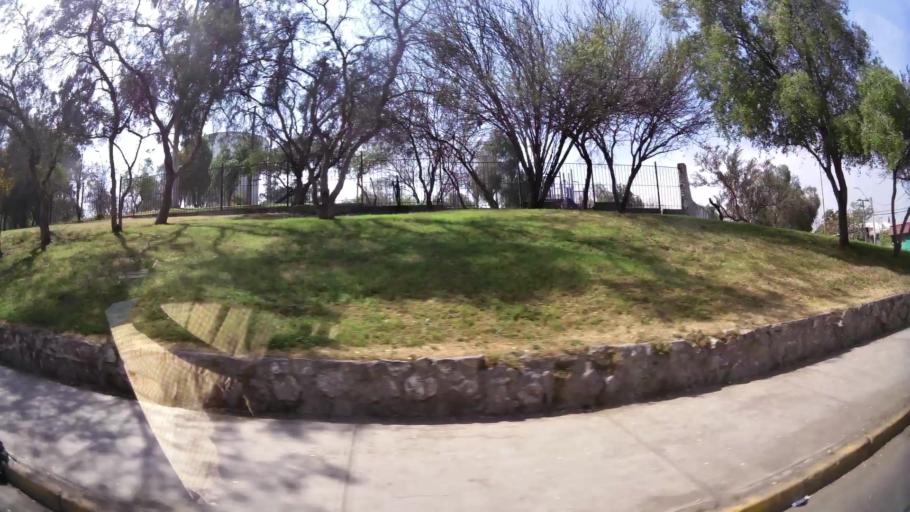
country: CL
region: Santiago Metropolitan
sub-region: Provincia de Santiago
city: Lo Prado
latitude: -33.4248
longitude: -70.7215
